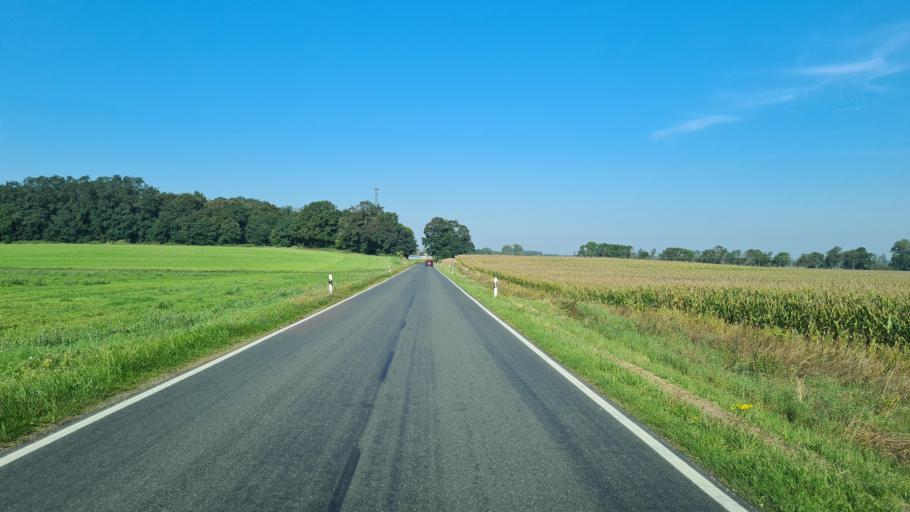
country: DE
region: Brandenburg
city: Friesack
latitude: 52.7353
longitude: 12.6015
